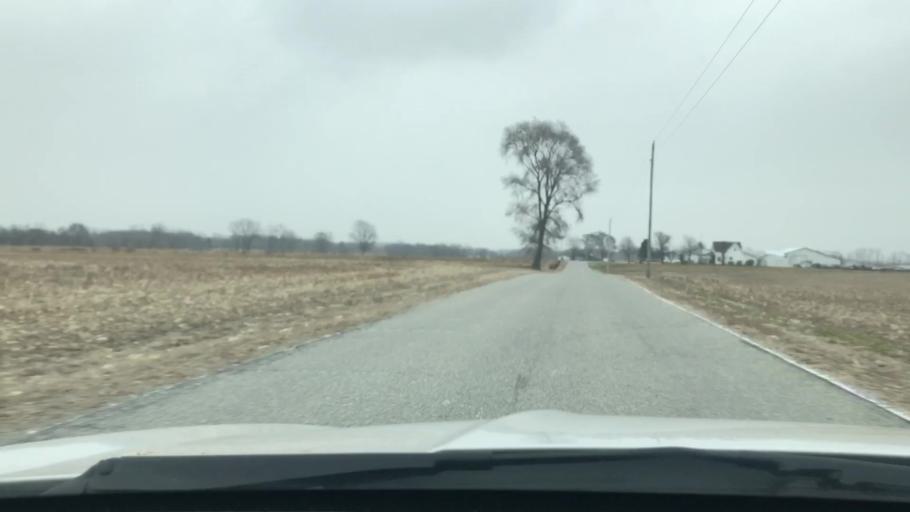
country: US
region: Indiana
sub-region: Fulton County
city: Akron
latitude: 41.0405
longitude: -86.0930
